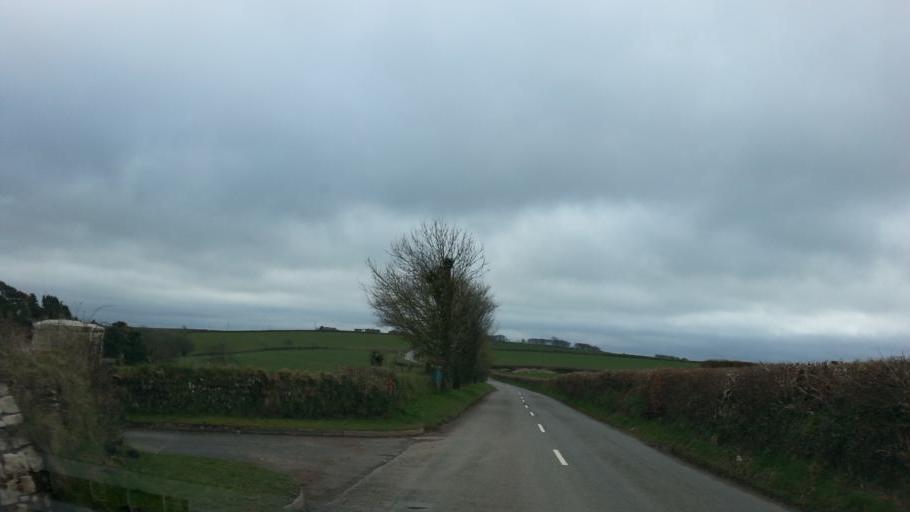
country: GB
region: England
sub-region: Devon
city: Barnstaple
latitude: 51.1289
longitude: -4.0125
